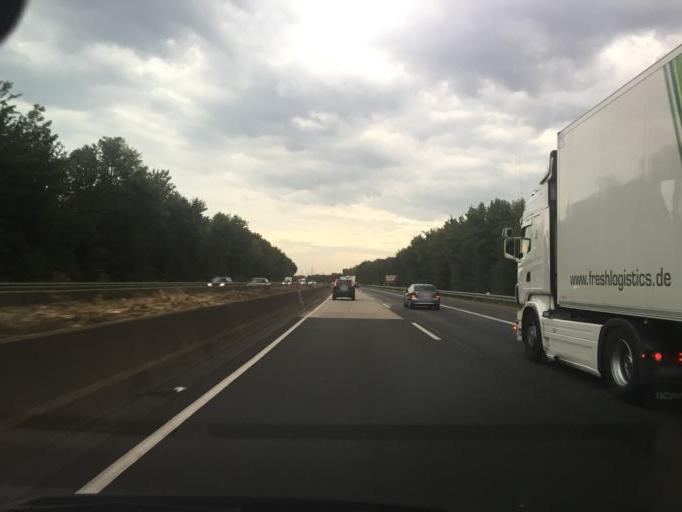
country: DE
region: North Rhine-Westphalia
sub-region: Regierungsbezirk Koln
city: Elsdorf
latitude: 50.9590
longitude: 6.5752
